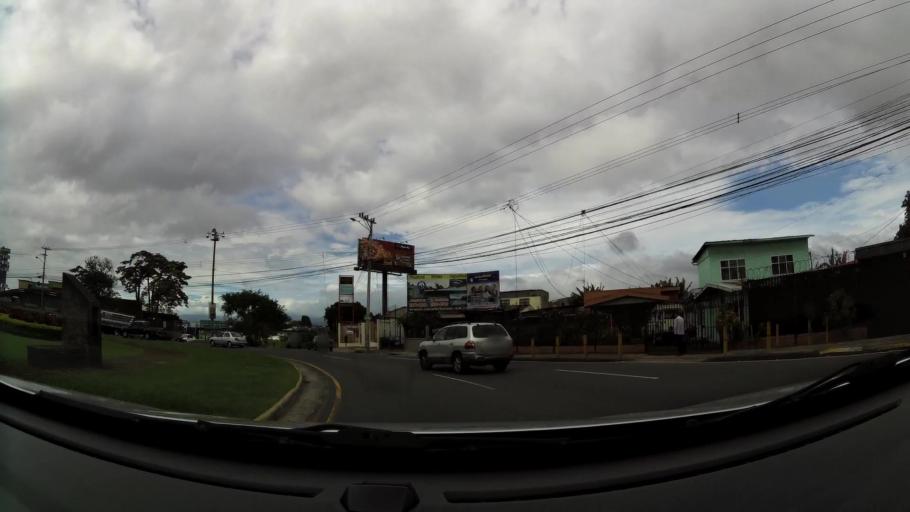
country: CR
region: San Jose
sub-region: Canton de Goicoechea
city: Guadalupe
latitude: 9.9395
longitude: -84.0545
